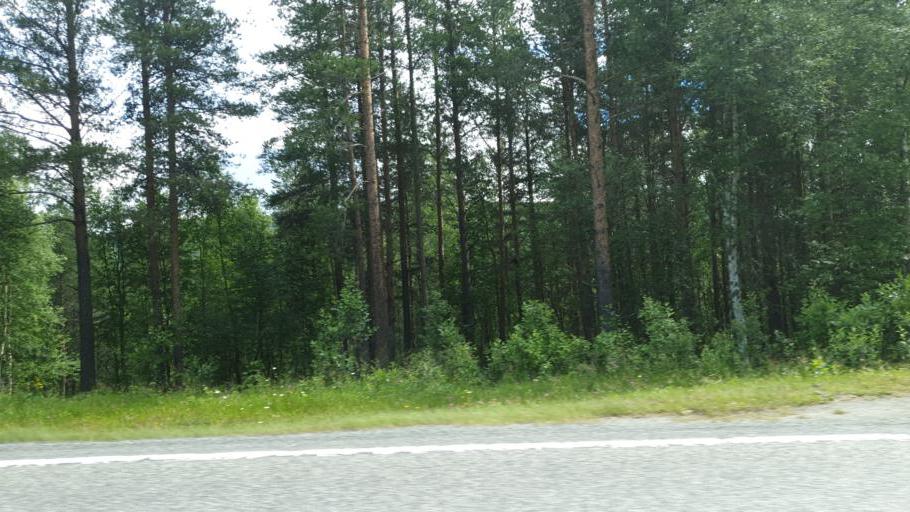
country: NO
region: Sor-Trondelag
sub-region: Rennebu
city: Berkak
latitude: 62.6720
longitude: 9.9105
